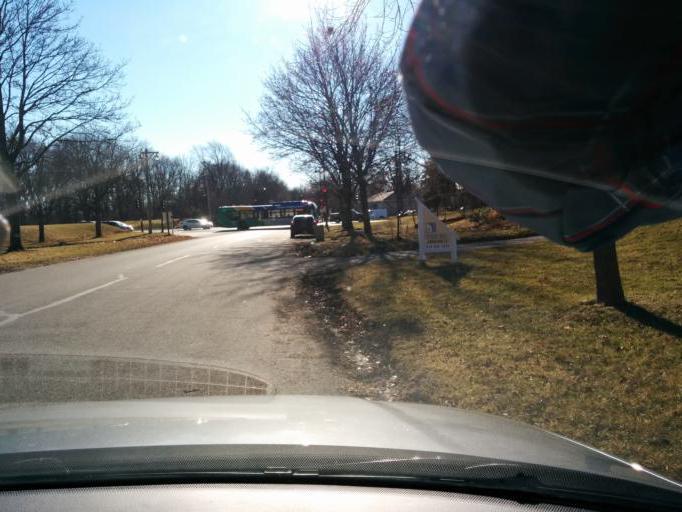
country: US
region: Wisconsin
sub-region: Milwaukee County
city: Glendale
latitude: 43.1196
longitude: -87.9232
